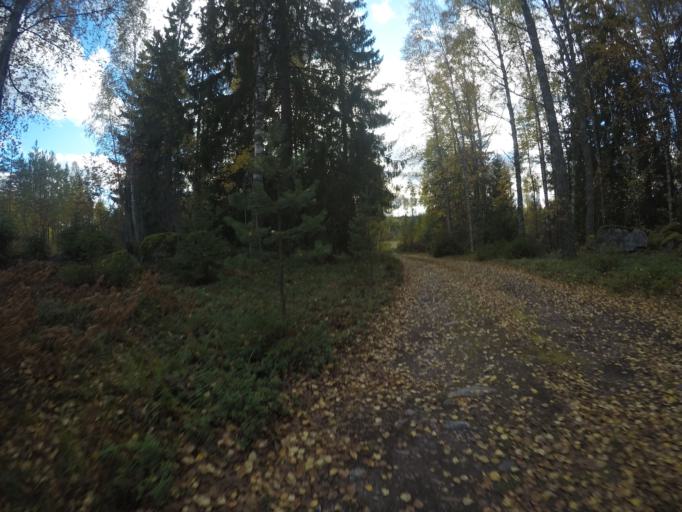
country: SE
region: Vaestmanland
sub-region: Arboga Kommun
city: Tyringe
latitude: 59.3541
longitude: 15.9581
